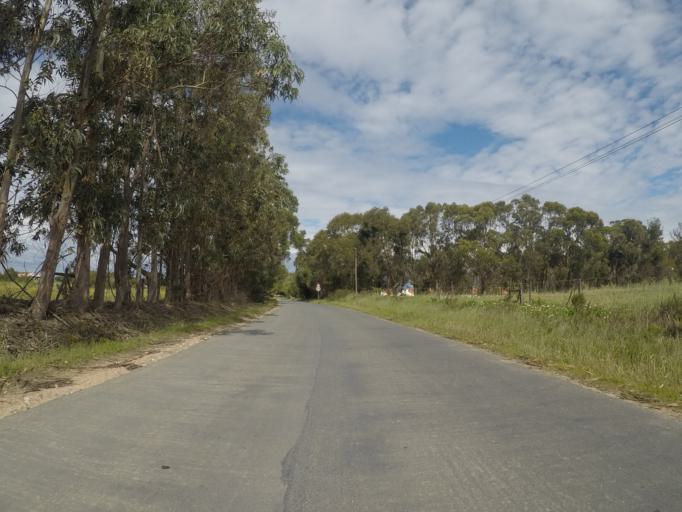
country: PT
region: Beja
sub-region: Odemira
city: Sao Teotonio
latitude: 37.4944
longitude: -8.7851
